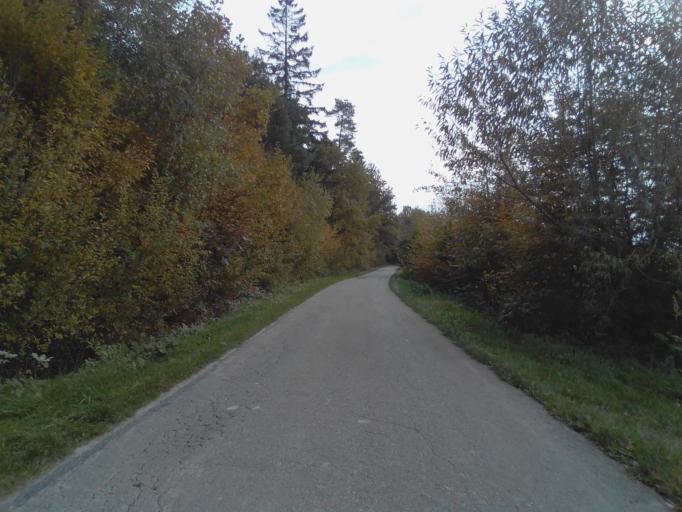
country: PL
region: Subcarpathian Voivodeship
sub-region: Powiat rzeszowski
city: Straszydle
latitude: 49.8627
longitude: 21.9719
